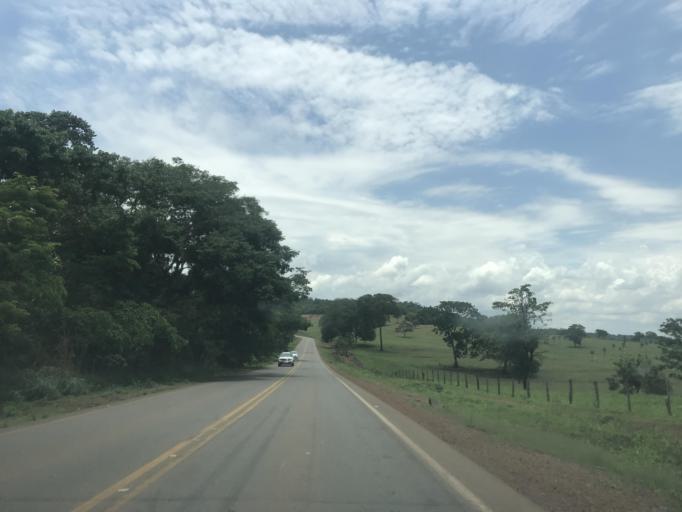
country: BR
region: Goias
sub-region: Vianopolis
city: Vianopolis
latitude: -16.7104
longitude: -48.3995
